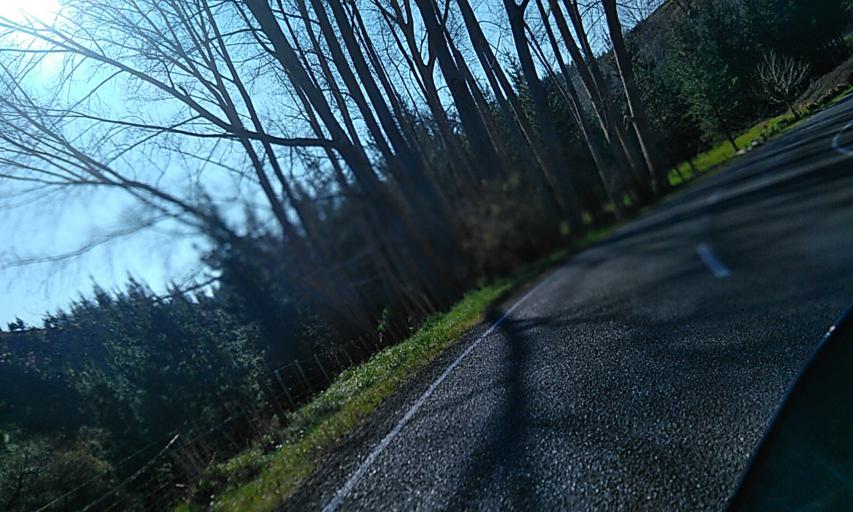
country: NZ
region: Gisborne
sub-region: Gisborne District
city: Gisborne
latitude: -38.5621
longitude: 178.0239
